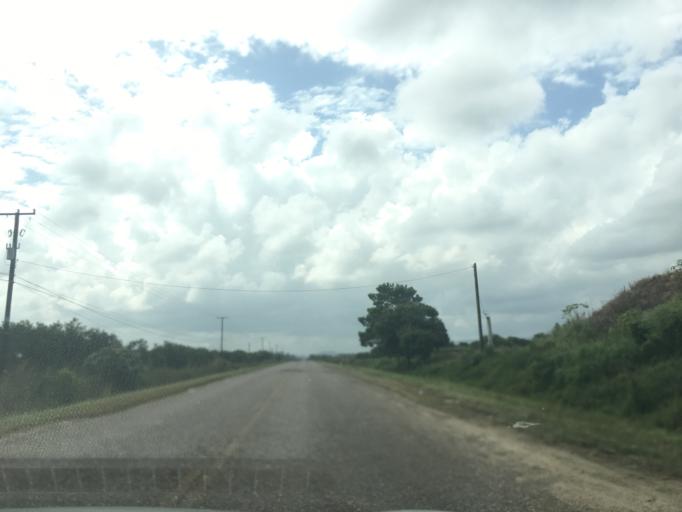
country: BZ
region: Stann Creek
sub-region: Dangriga
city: Dangriga
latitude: 16.9779
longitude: -88.2971
